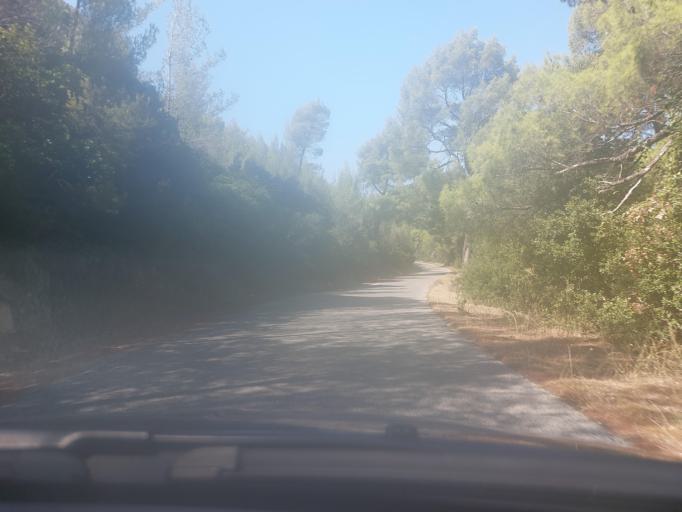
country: HR
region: Dubrovacko-Neretvanska
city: Smokvica
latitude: 42.7472
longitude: 16.8411
